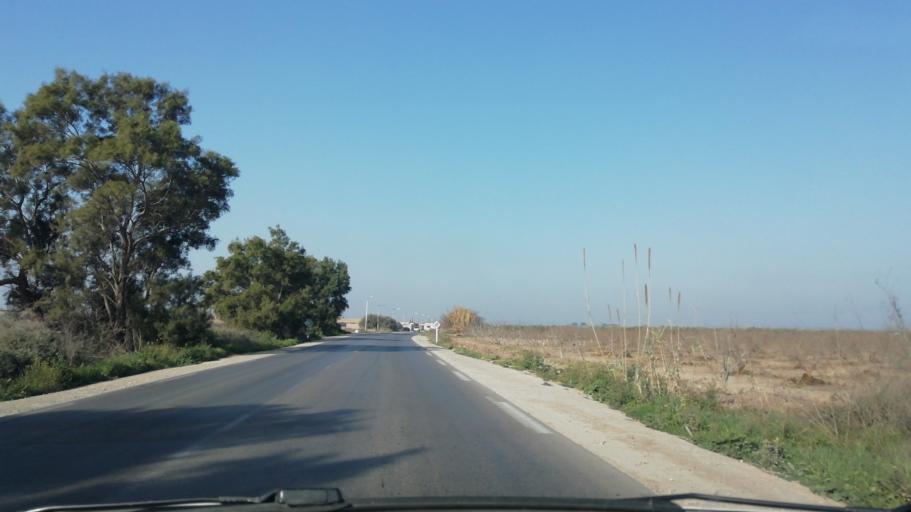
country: DZ
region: Mostaganem
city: Mostaganem
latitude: 35.7591
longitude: 0.0691
